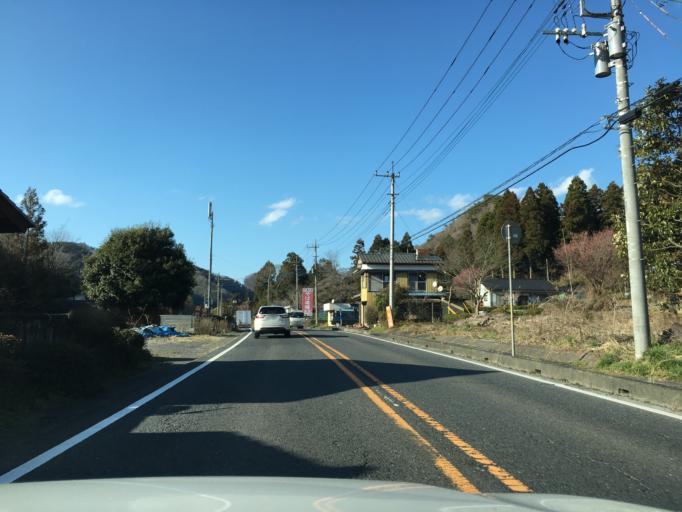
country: JP
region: Ibaraki
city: Daigo
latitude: 36.6760
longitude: 140.3903
